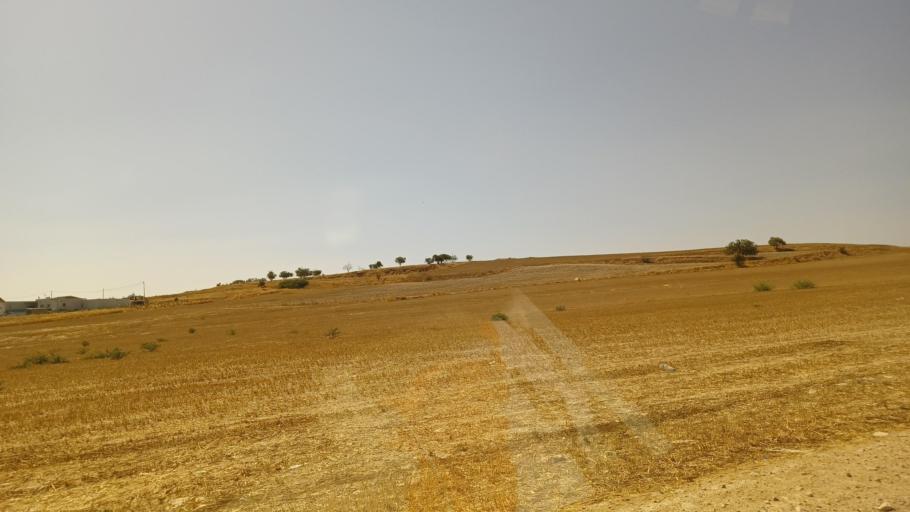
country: CY
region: Larnaka
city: Athienou
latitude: 35.0476
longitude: 33.5413
